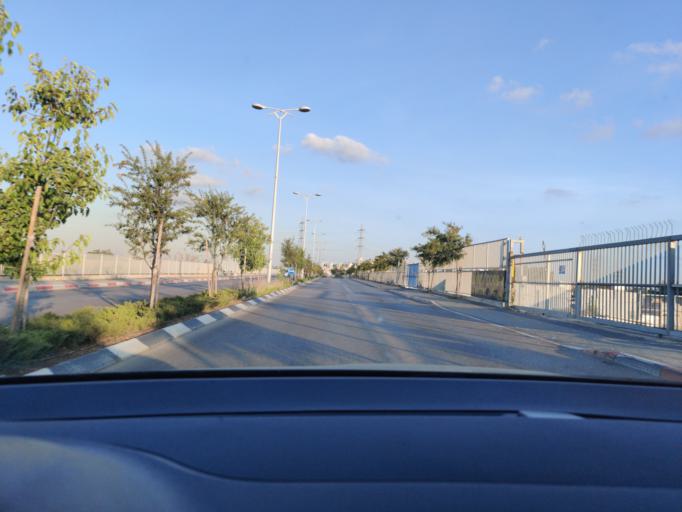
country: IL
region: Haifa
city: Hadera
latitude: 32.4417
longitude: 34.9350
